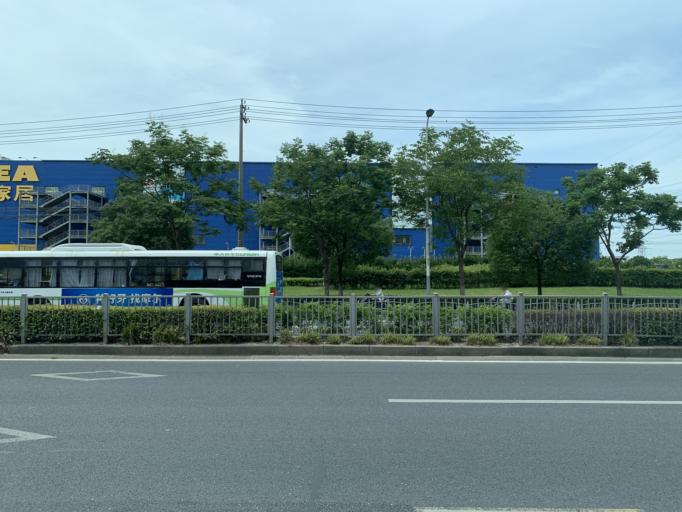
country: CN
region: Shanghai Shi
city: Kangqiao
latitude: 31.1623
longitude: 121.5596
